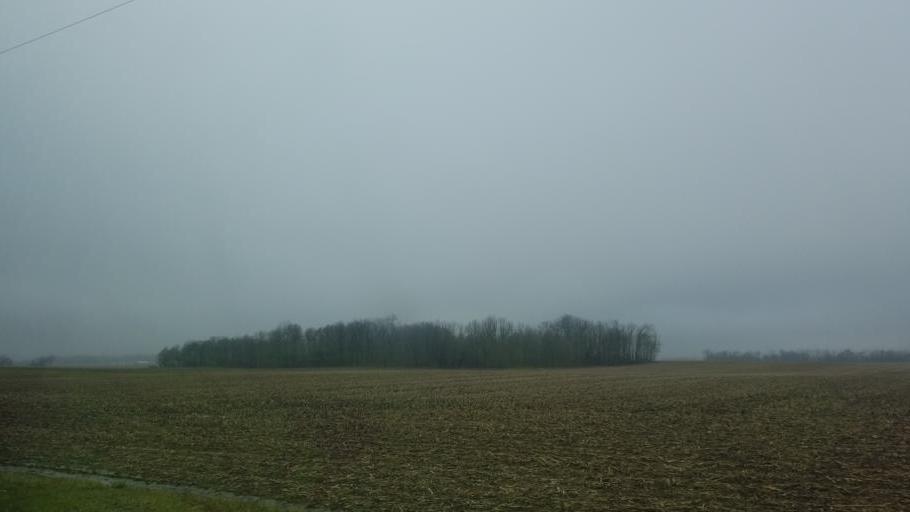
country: US
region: Ohio
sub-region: Champaign County
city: North Lewisburg
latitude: 40.2421
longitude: -83.5465
